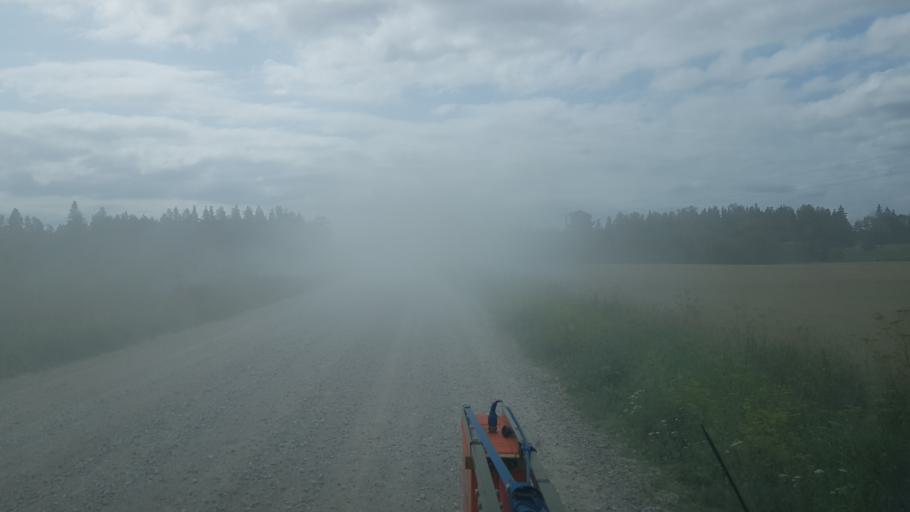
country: EE
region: Paernumaa
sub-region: Halinga vald
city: Parnu-Jaagupi
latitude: 58.5816
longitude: 24.4059
